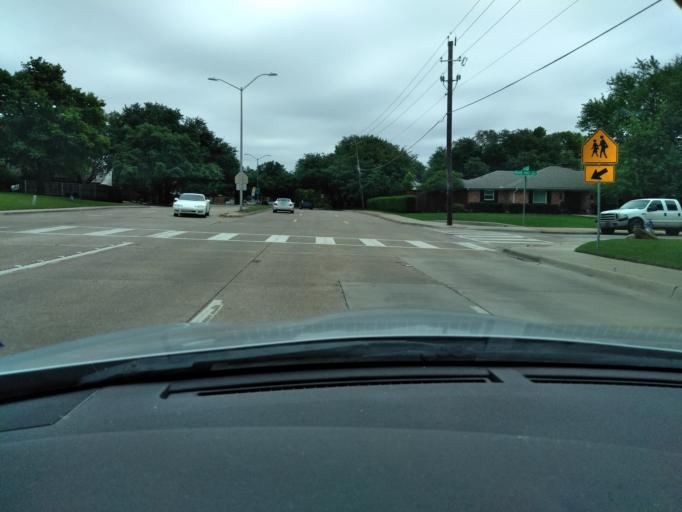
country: US
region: Texas
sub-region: Dallas County
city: Addison
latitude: 32.9819
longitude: -96.7859
